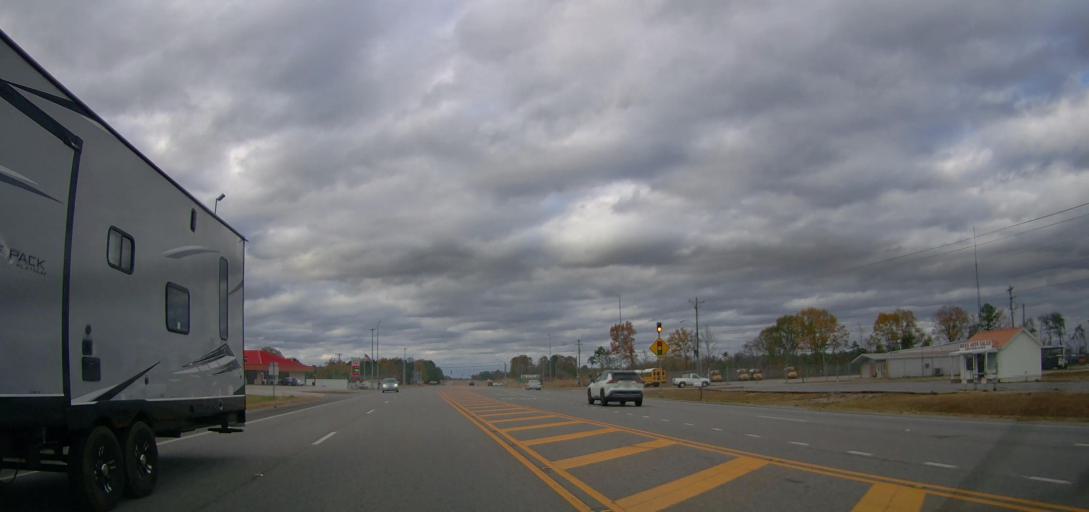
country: US
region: Alabama
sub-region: Lawrence County
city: Moulton
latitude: 34.5129
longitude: -87.2904
